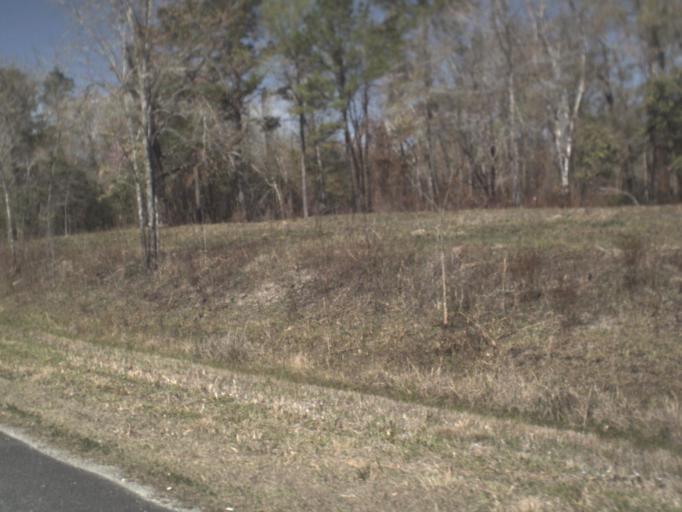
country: US
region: Florida
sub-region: Wakulla County
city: Crawfordville
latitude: 30.2444
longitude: -84.3147
